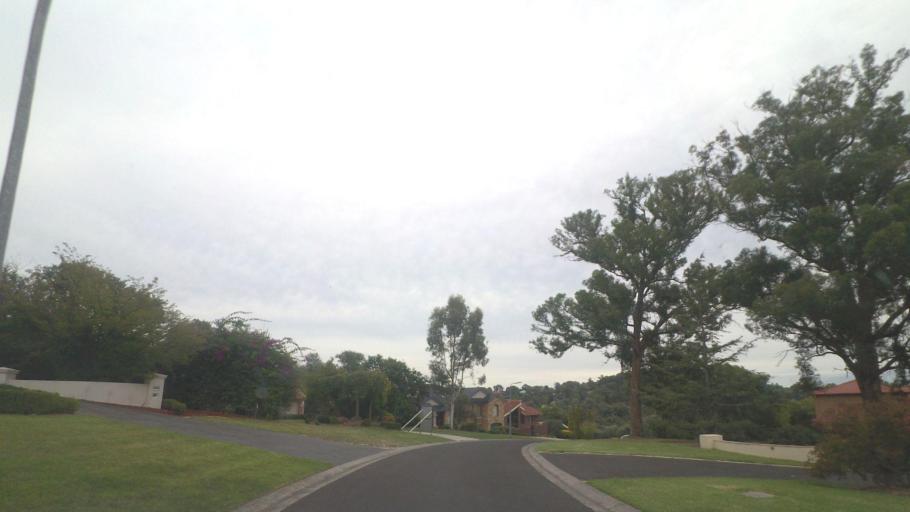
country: AU
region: Victoria
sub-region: Nillumbik
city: North Warrandyte
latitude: -37.7418
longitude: 145.1869
